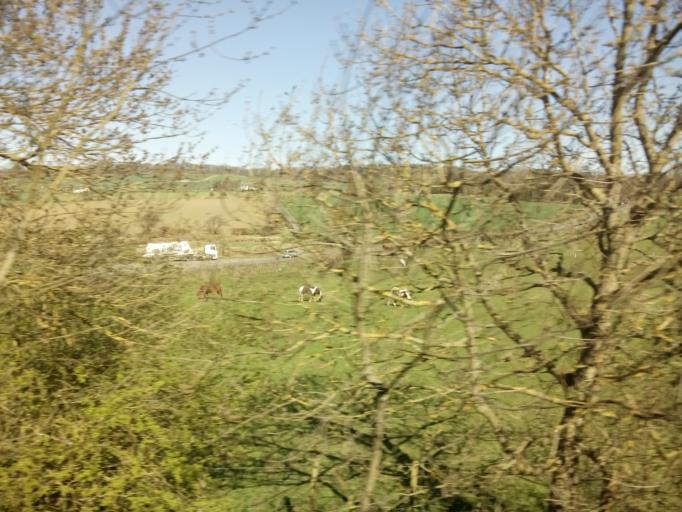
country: GB
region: Scotland
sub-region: Fife
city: Aberdour
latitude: 56.0535
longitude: -3.3172
